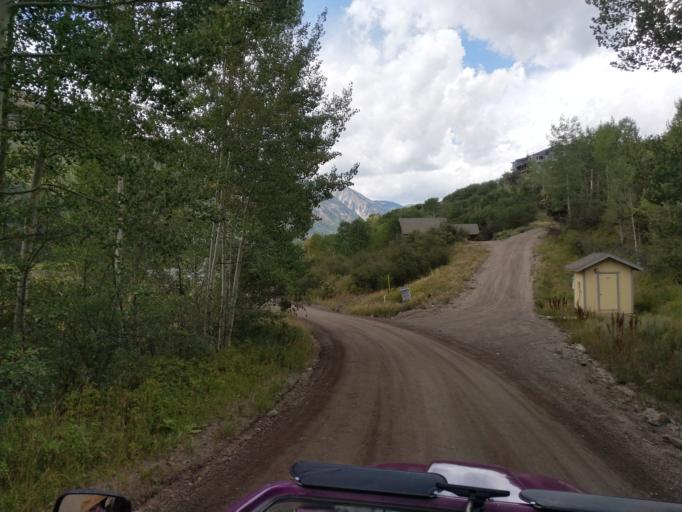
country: US
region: Colorado
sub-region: Pitkin County
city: Snowmass Village
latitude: 39.0722
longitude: -107.1732
